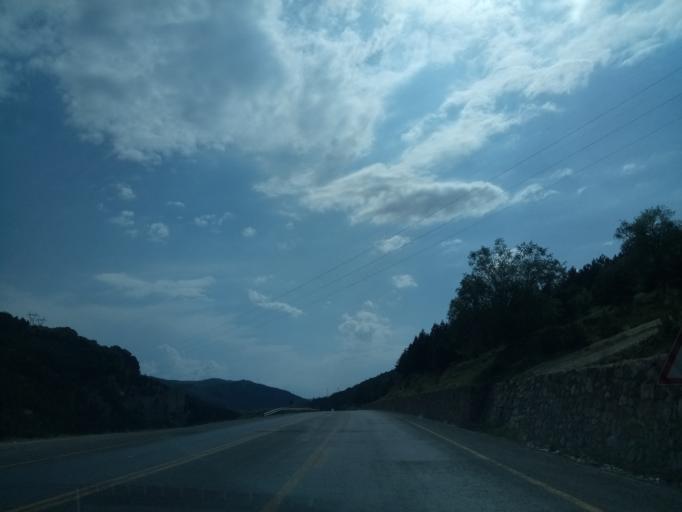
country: TR
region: Konya
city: Aksehir
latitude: 38.2778
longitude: 31.4282
